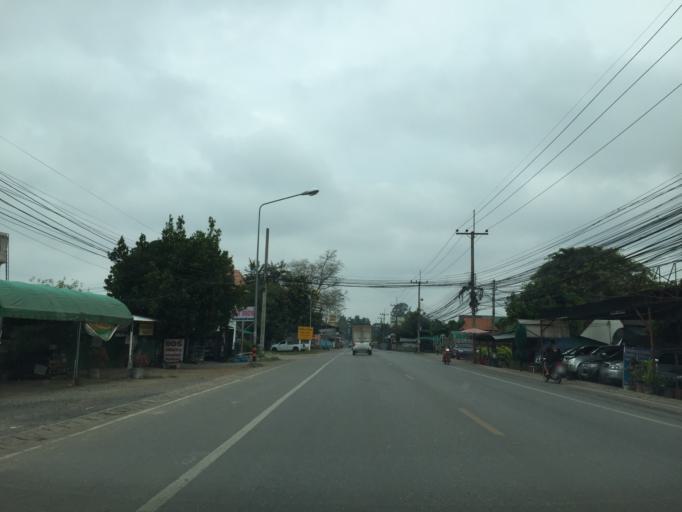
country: TH
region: Lamphun
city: Lamphun
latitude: 18.5818
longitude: 99.0670
